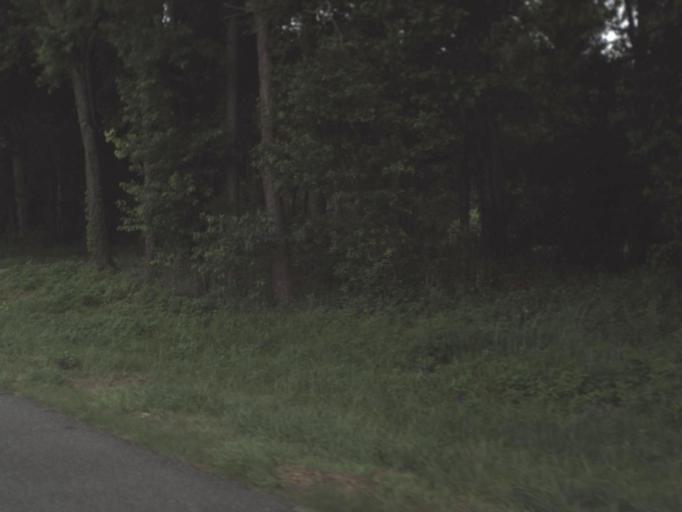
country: US
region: Florida
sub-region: Alachua County
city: Archer
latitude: 29.5582
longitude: -82.5333
